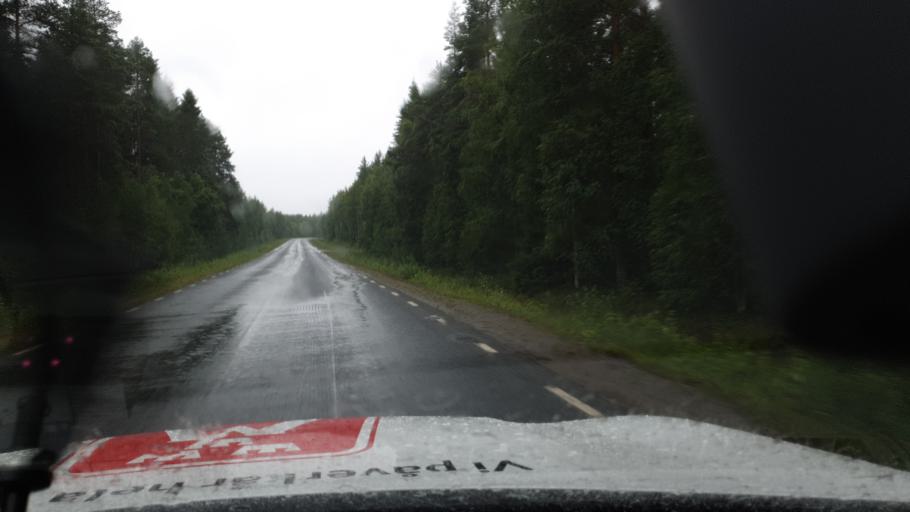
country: SE
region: Vaesterbotten
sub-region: Skelleftea Kommun
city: Soedra Bergsbyn
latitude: 64.5853
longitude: 21.0197
